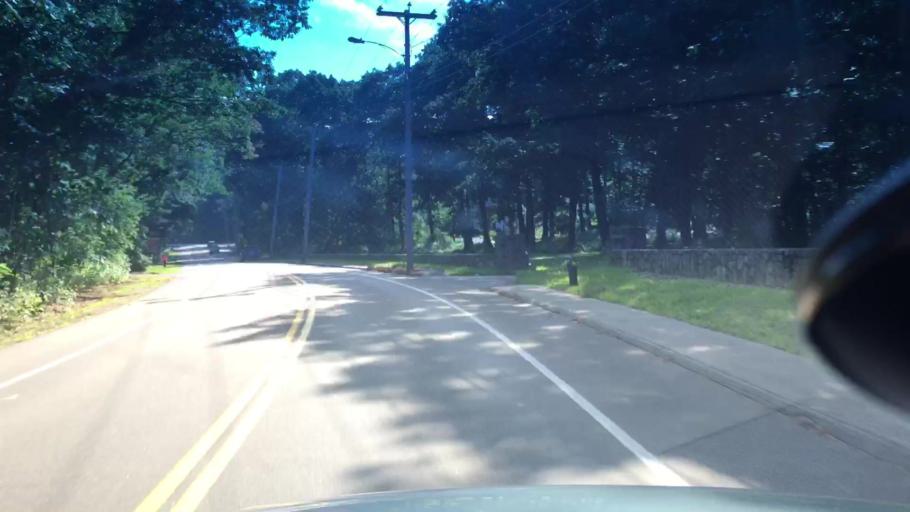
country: US
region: Maine
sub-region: York County
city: York Harbor
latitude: 43.1464
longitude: -70.6265
